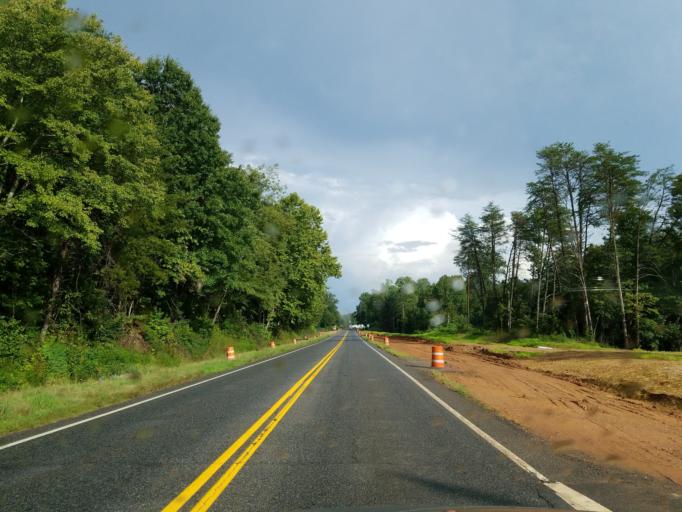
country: US
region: Georgia
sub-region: White County
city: Cleveland
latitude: 34.6105
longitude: -83.7747
